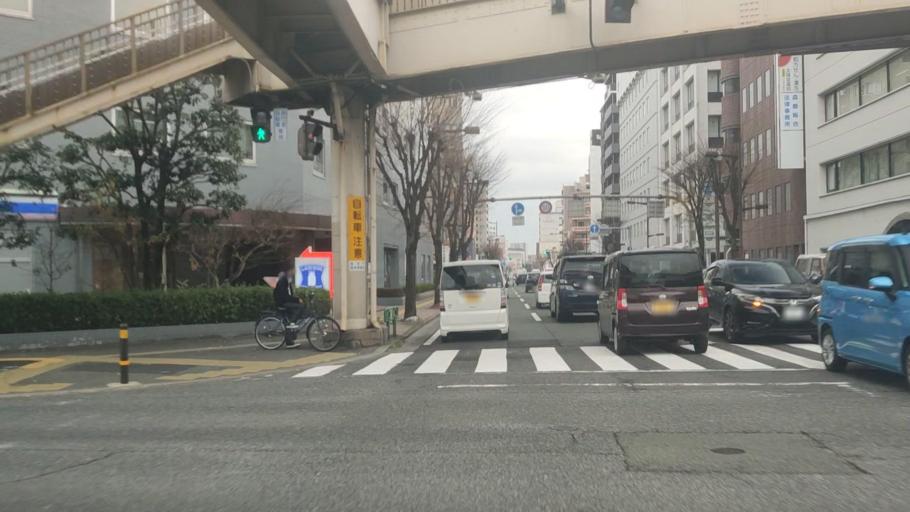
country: JP
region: Kumamoto
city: Kumamoto
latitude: 32.7996
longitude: 130.7177
